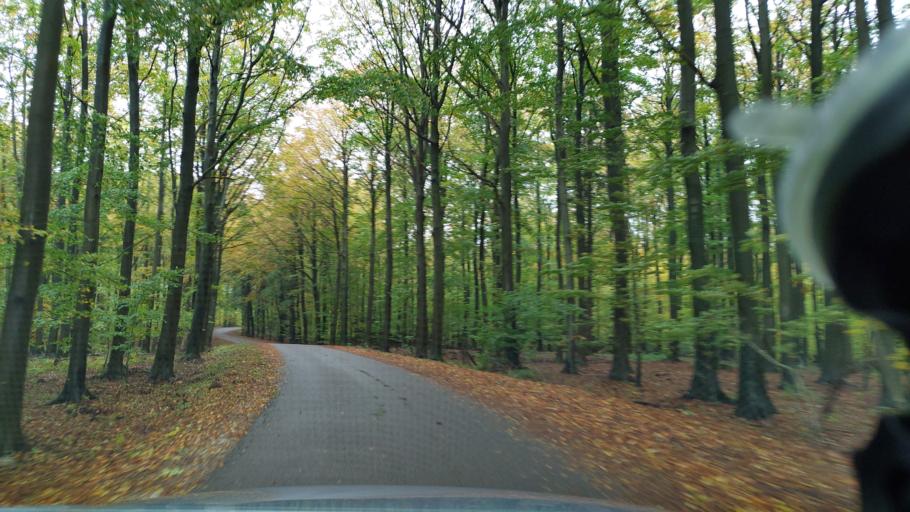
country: DK
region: Zealand
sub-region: Faxe Kommune
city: Ronnede
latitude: 55.2430
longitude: 11.9527
